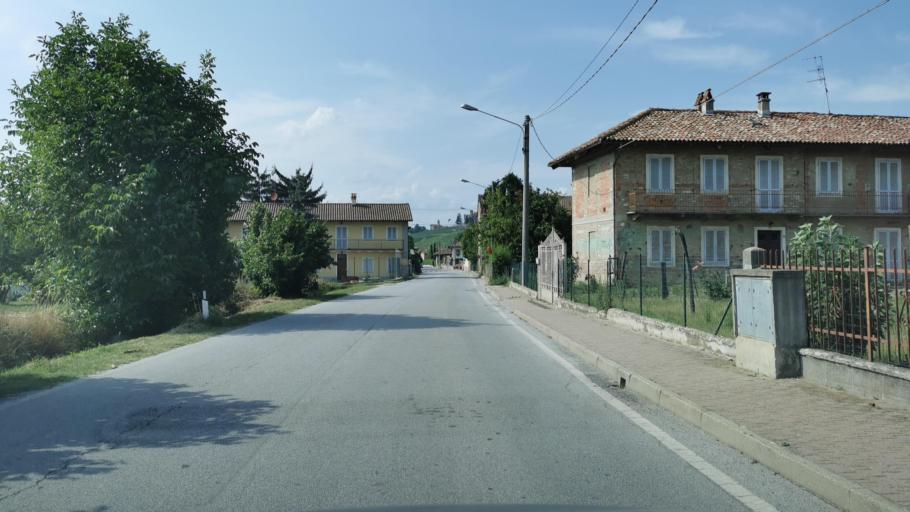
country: IT
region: Piedmont
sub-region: Provincia di Cuneo
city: Grinzane Cavour
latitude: 44.6423
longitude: 8.0001
